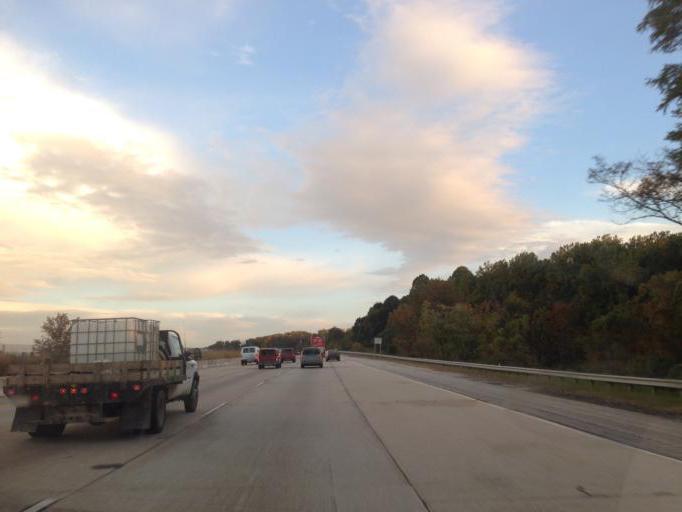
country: US
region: Maryland
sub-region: Baltimore County
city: Garrison
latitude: 39.3785
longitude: -76.7529
